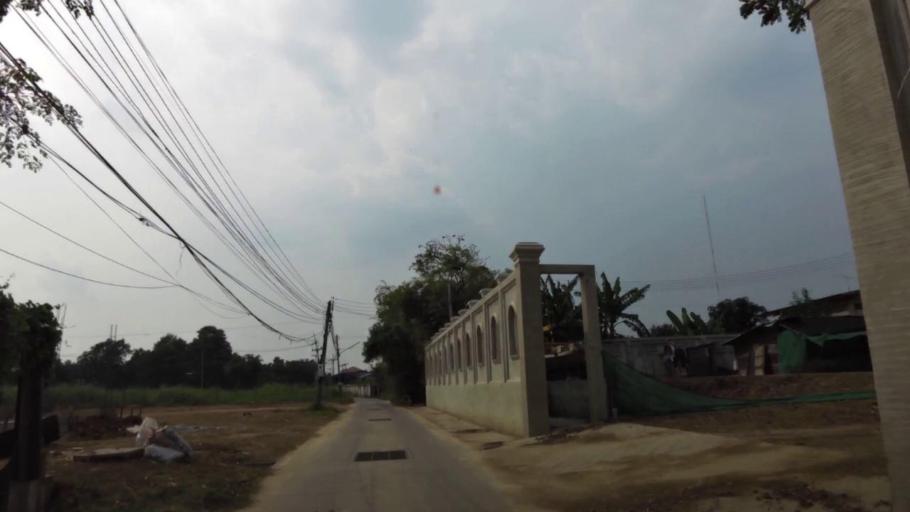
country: TH
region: Phra Nakhon Si Ayutthaya
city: Phra Nakhon Si Ayutthaya
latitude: 14.3424
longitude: 100.5785
